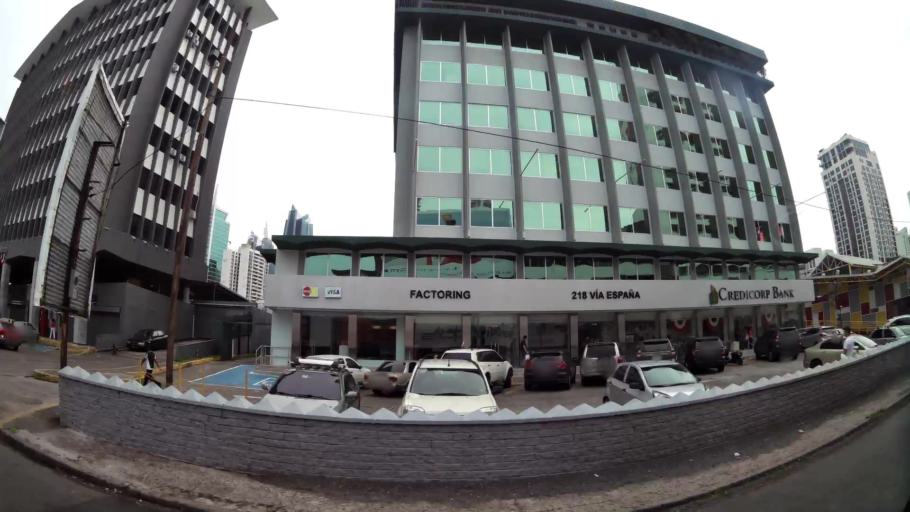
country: PA
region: Panama
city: Panama
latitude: 8.9855
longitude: -79.5248
